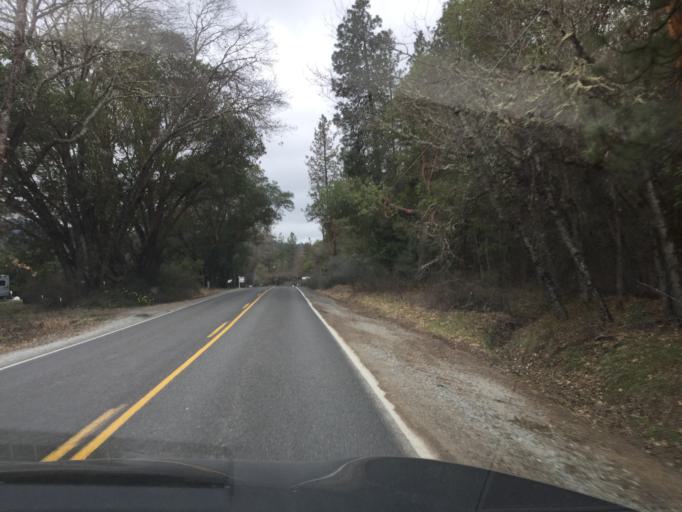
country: US
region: Oregon
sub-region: Jackson County
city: Gold Hill
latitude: 42.3963
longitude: -123.0052
